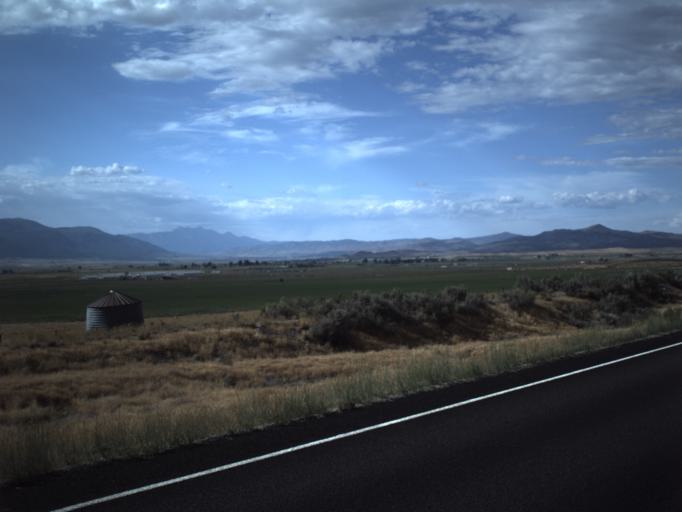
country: US
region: Utah
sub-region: Sanpete County
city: Ephraim
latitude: 39.4317
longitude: -111.5539
